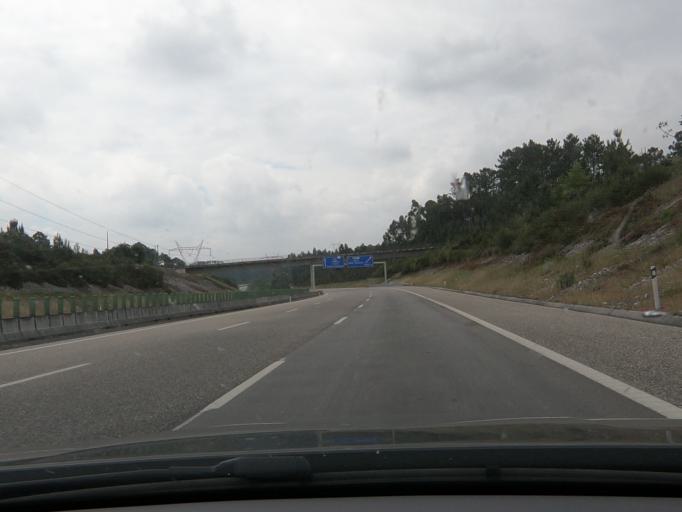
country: PT
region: Leiria
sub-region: Pombal
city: Lourical
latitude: 39.9577
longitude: -8.7748
